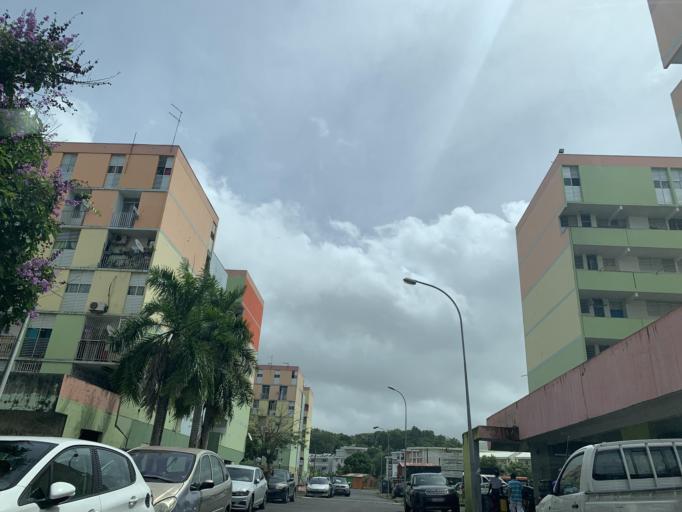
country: GP
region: Guadeloupe
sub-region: Guadeloupe
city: Pointe-a-Pitre
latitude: 16.2398
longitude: -61.5305
